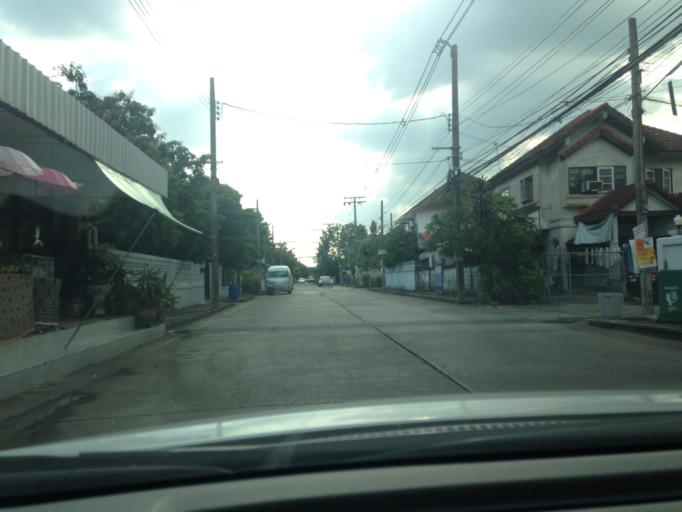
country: TH
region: Bangkok
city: Khan Na Yao
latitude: 13.8391
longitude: 100.6446
